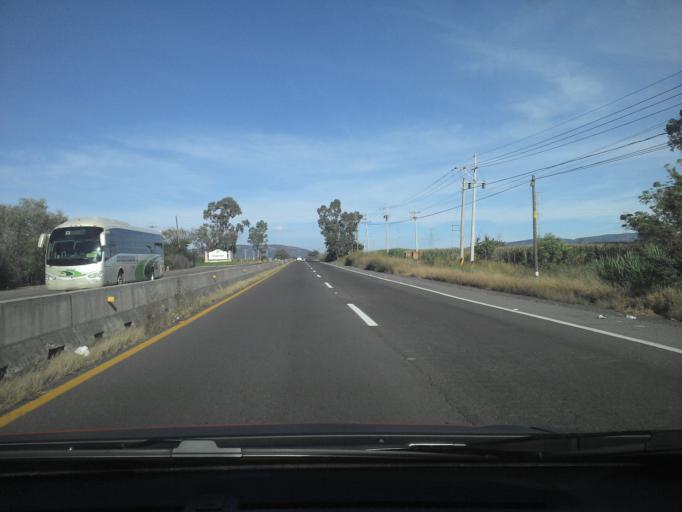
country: MX
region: Jalisco
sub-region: Tala
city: Los Ruisenores
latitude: 20.7082
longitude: -103.6731
